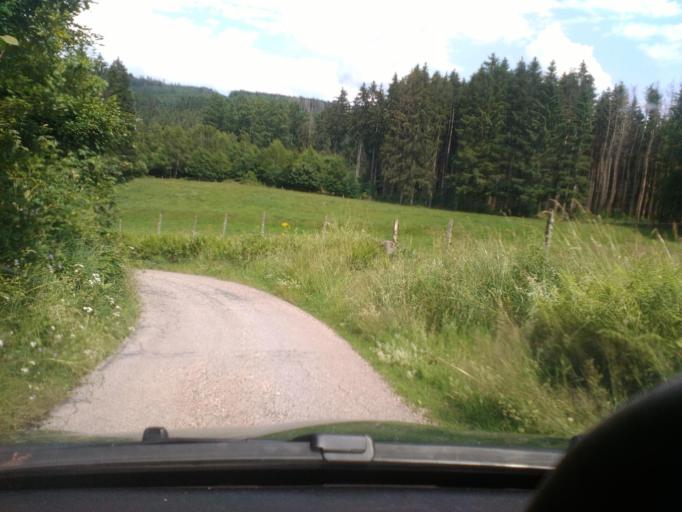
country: FR
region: Lorraine
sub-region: Departement des Vosges
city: Senones
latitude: 48.3744
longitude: 7.0472
